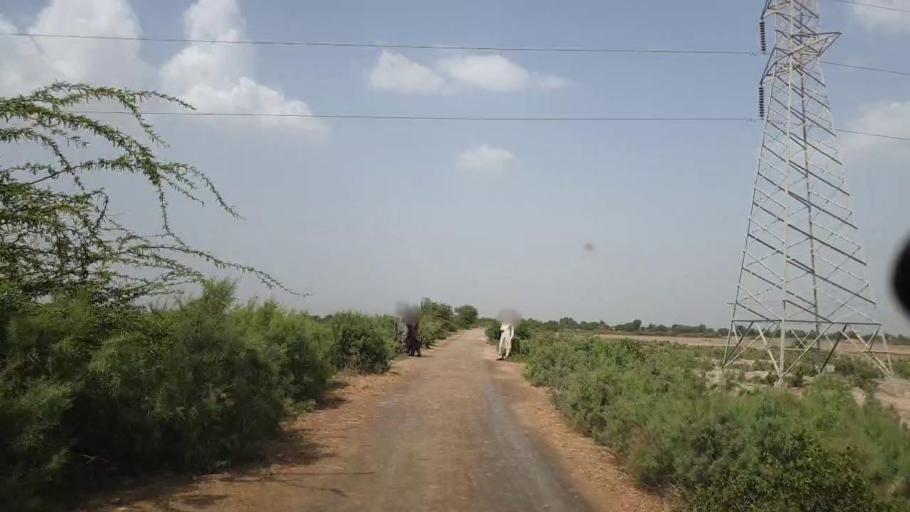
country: PK
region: Sindh
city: Tando Ghulam Ali
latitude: 25.0707
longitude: 68.8110
